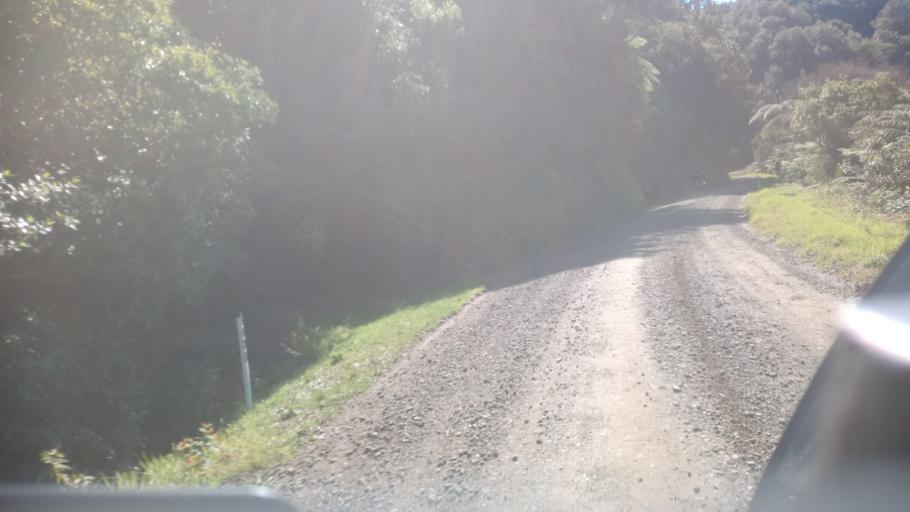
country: NZ
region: Bay of Plenty
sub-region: Opotiki District
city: Opotiki
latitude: -38.0386
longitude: 177.4417
